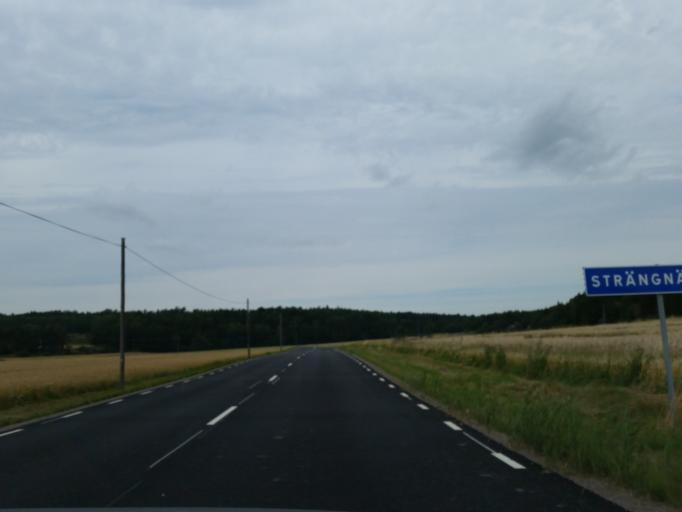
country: SE
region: Soedermanland
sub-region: Strangnas Kommun
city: Mariefred
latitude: 59.2561
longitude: 17.1776
